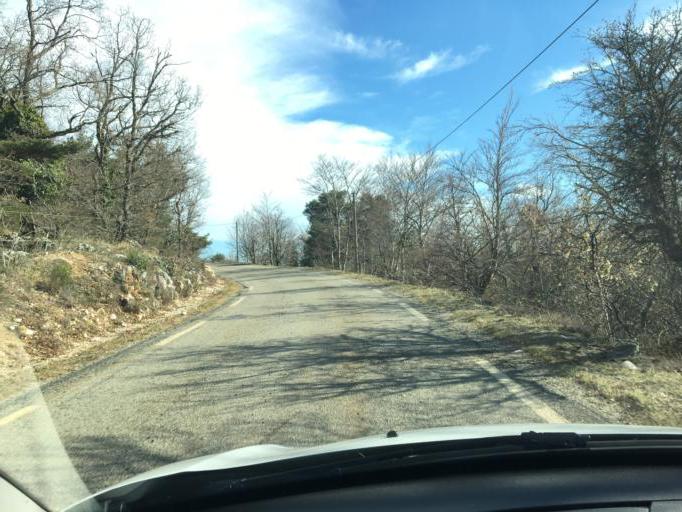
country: FR
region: Provence-Alpes-Cote d'Azur
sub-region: Departement du Vaucluse
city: Saint-Saturnin-les-Apt
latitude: 43.9751
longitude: 5.4628
